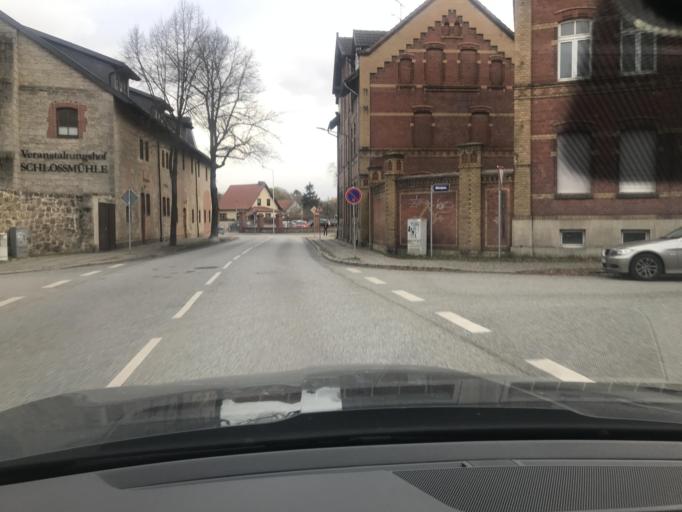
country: DE
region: Saxony-Anhalt
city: Quedlinburg
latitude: 51.7855
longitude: 11.1345
